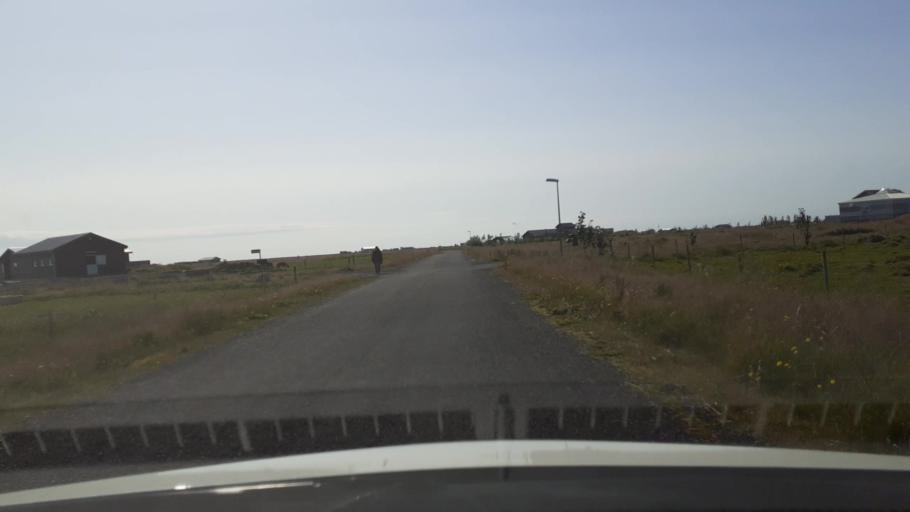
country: IS
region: South
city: Selfoss
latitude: 63.8935
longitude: -21.0860
